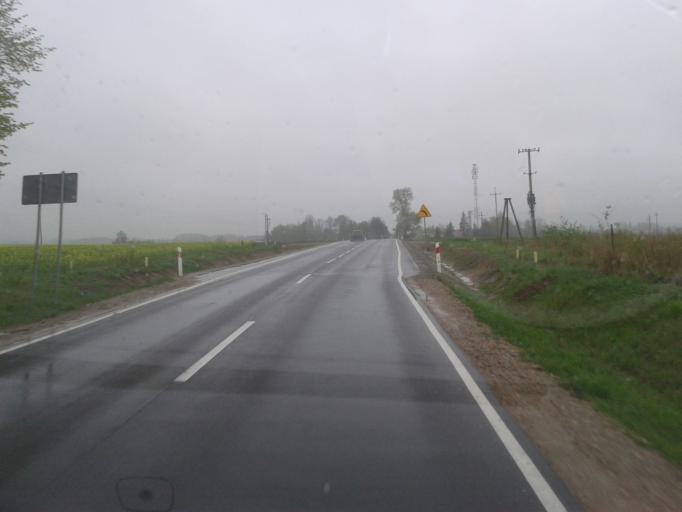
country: PL
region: Subcarpathian Voivodeship
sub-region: Powiat lubaczowski
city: Cieszanow
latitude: 50.2565
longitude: 23.1414
